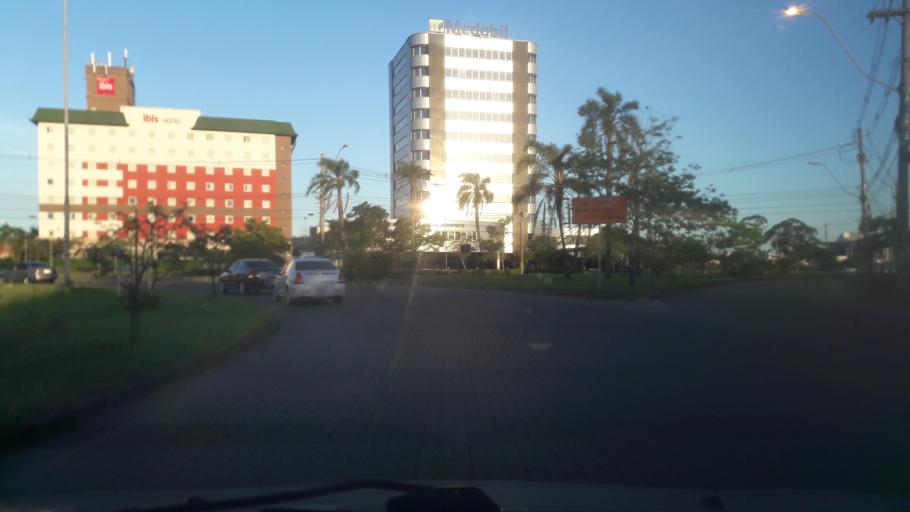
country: BR
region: Rio Grande do Sul
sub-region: Canoas
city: Canoas
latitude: -29.9880
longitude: -51.1716
